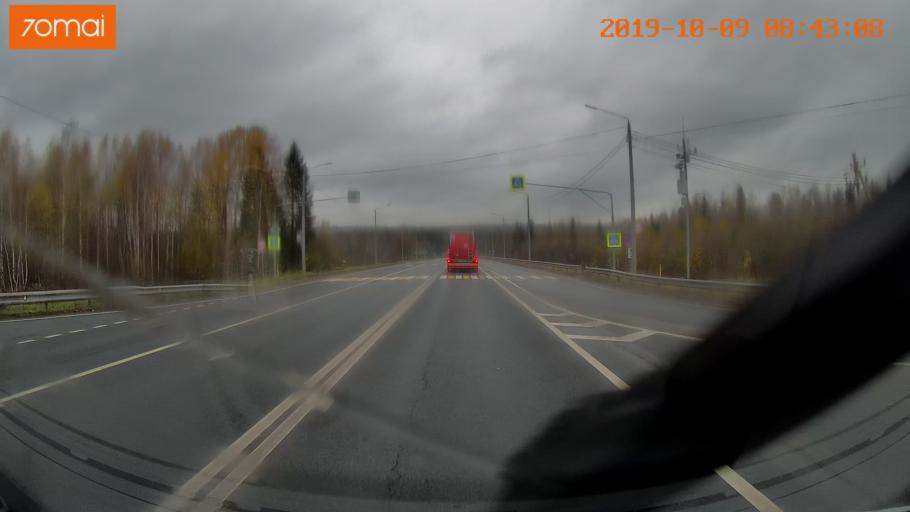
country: RU
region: Vologda
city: Gryazovets
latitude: 59.0214
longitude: 40.1157
